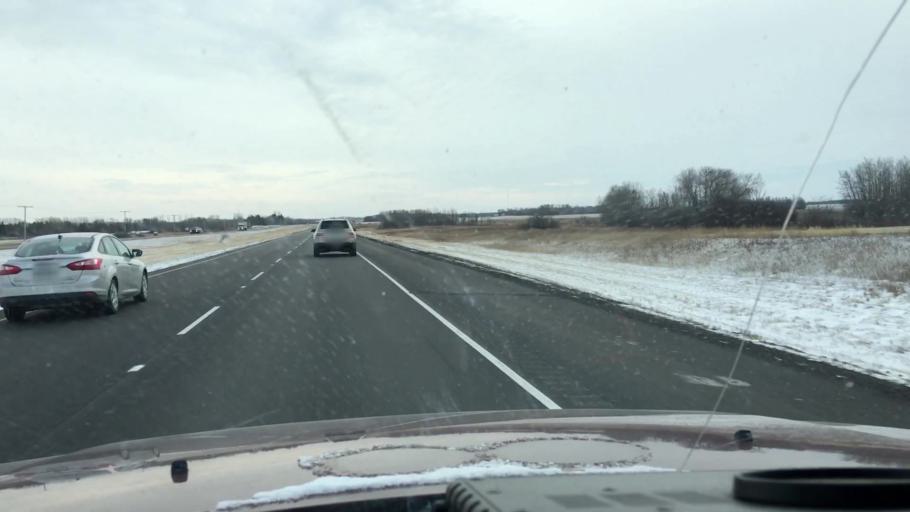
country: CA
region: Saskatchewan
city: Saskatoon
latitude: 52.0235
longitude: -106.5799
